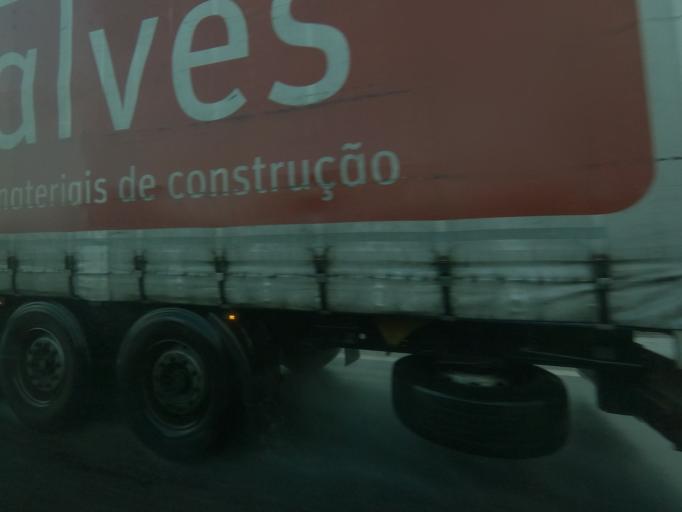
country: PT
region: Viana do Castelo
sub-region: Valenca
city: Valenza
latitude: 41.9925
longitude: -8.6441
